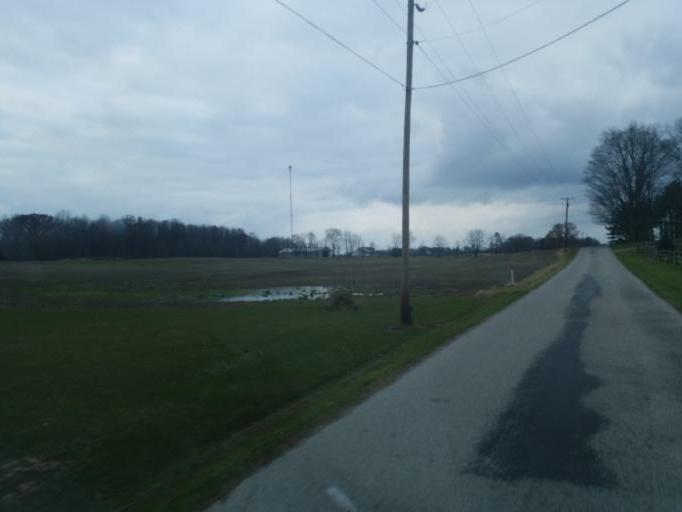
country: US
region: Ohio
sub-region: Morrow County
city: Mount Gilead
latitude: 40.5604
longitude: -82.7963
